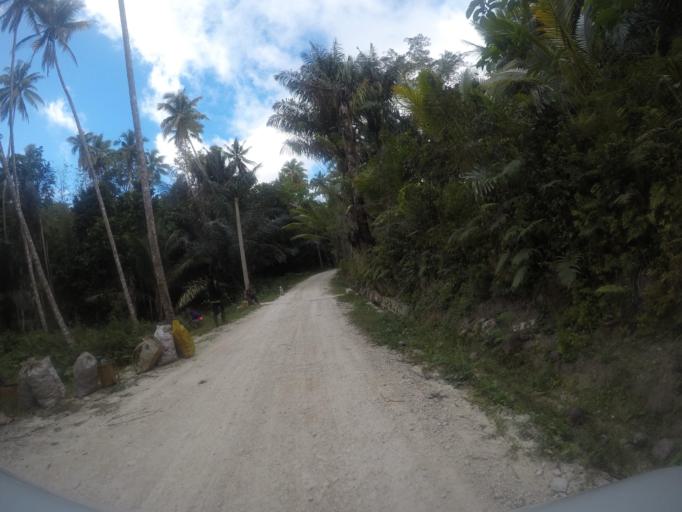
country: TL
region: Lautem
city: Lospalos
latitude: -8.5265
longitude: 126.9358
